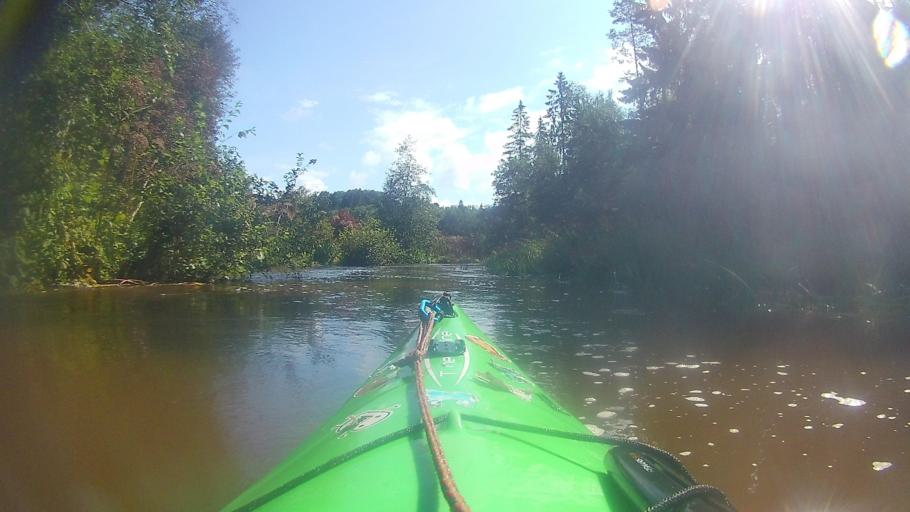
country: LV
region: Talsu Rajons
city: Sabile
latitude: 57.0012
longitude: 22.6017
